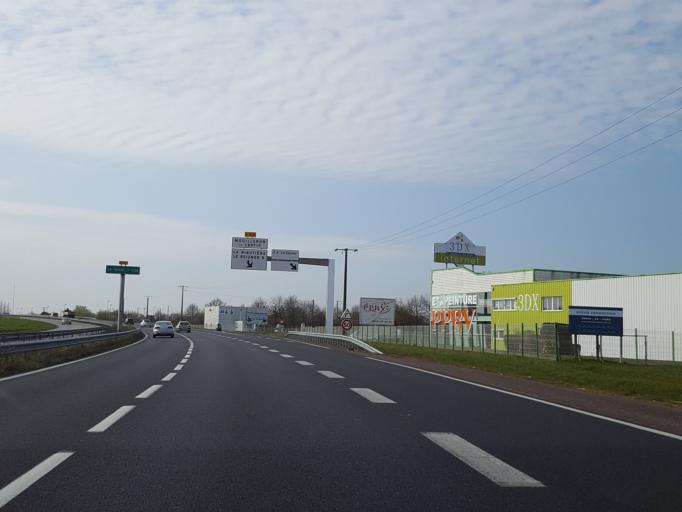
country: FR
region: Pays de la Loire
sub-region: Departement de la Vendee
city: Mouilleron-le-Captif
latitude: 46.7350
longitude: -1.4323
